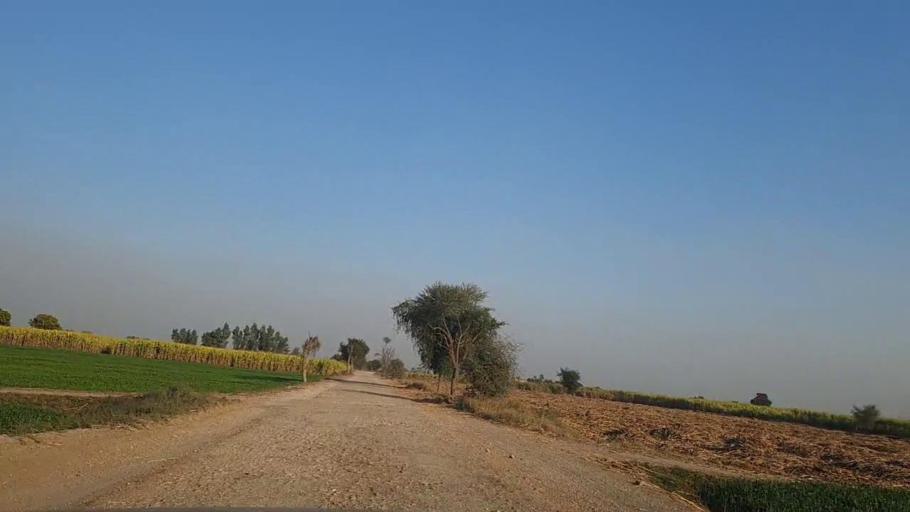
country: PK
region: Sindh
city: Sakrand
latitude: 26.3052
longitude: 68.1320
